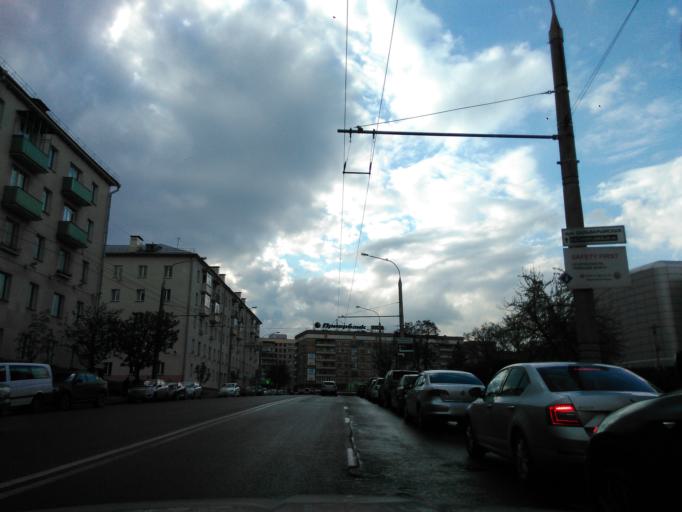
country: BY
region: Minsk
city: Minsk
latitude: 53.9043
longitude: 27.5431
